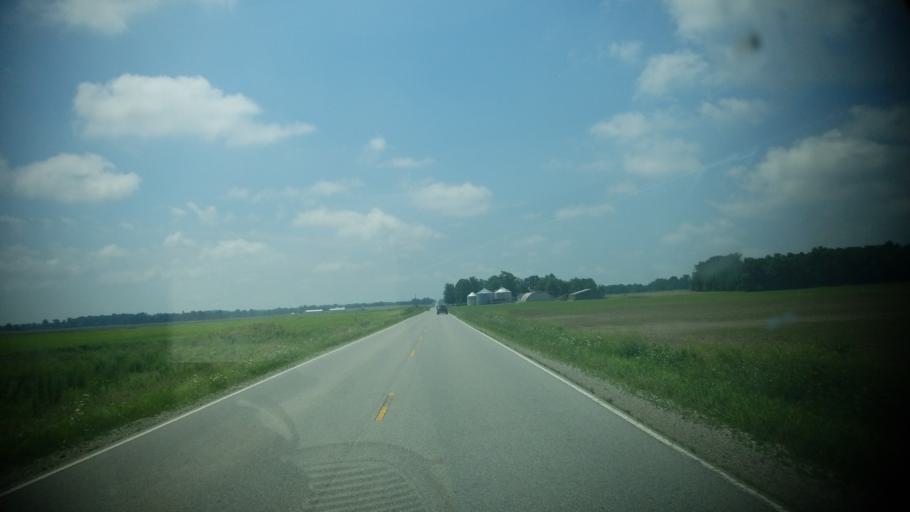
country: US
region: Illinois
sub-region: Wayne County
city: Fairfield
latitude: 38.4584
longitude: -88.3490
